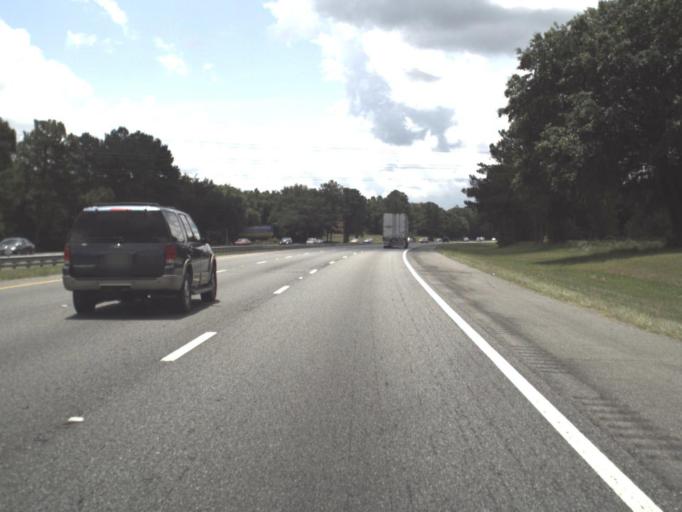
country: US
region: Florida
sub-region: Columbia County
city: Five Points
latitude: 30.2205
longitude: -82.7116
